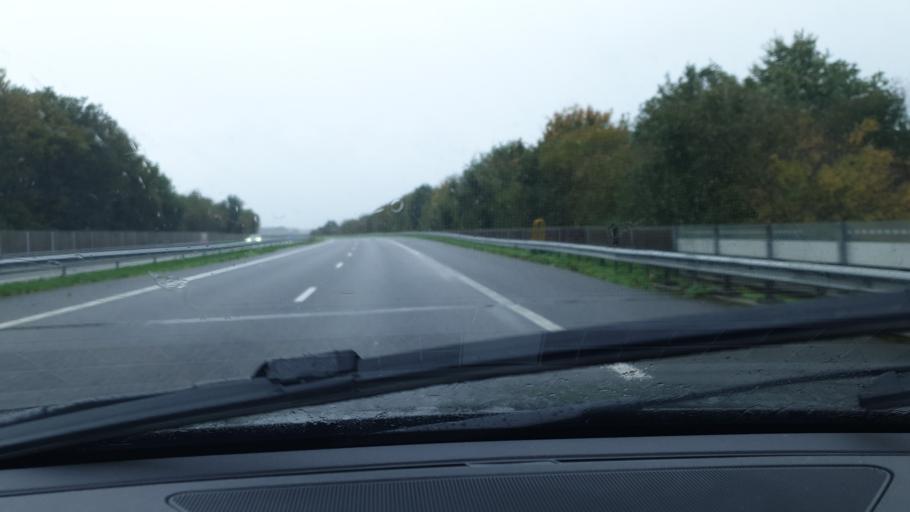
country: NL
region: Limburg
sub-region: Gemeente Venray
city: Venray
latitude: 51.4899
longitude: 6.0400
